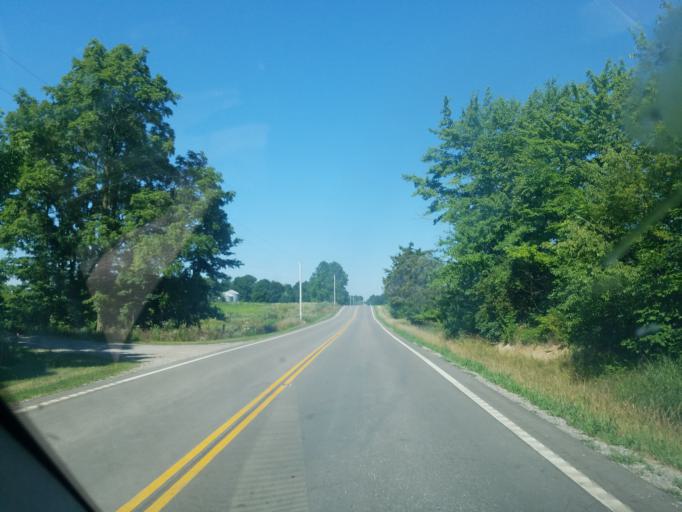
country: US
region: Ohio
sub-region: Logan County
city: Northwood
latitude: 40.4537
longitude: -83.7402
